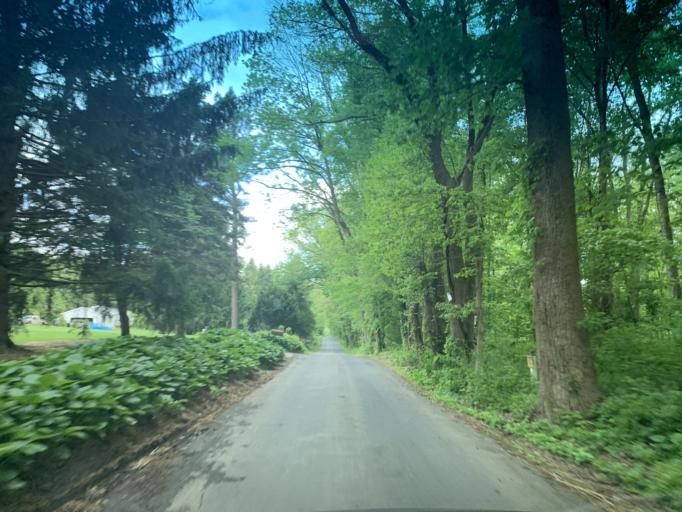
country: US
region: Maryland
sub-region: Cecil County
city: Rising Sun
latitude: 39.6885
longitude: -76.1450
